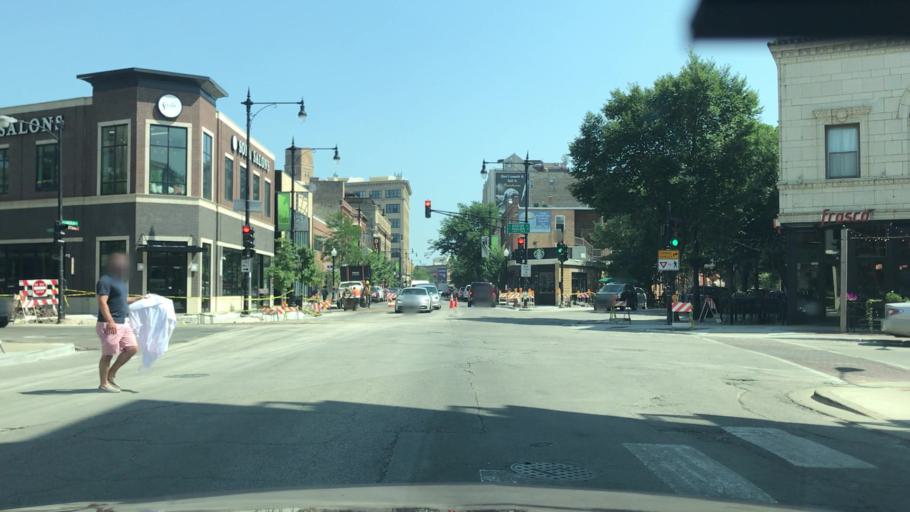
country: US
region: Illinois
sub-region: Cook County
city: Lincolnwood
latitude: 41.9436
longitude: -87.6714
